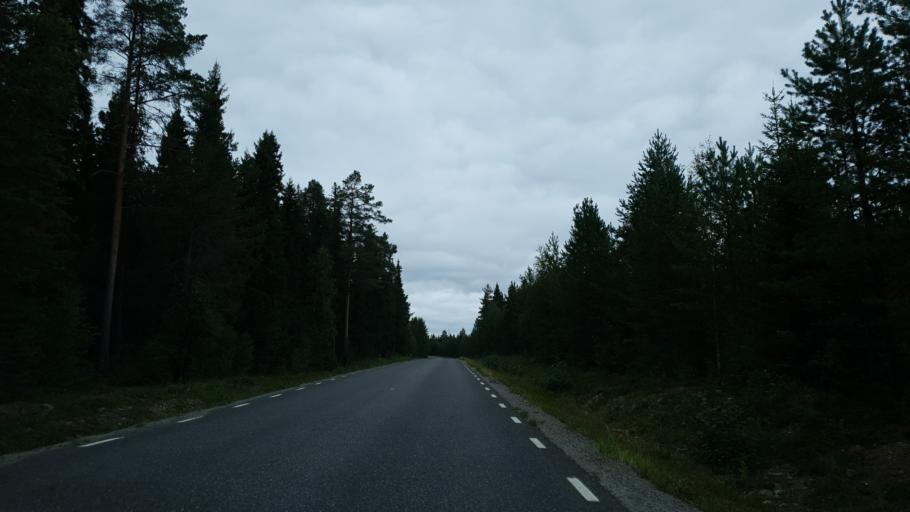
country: SE
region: Vaesterbotten
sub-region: Skelleftea Kommun
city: Viken
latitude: 64.8037
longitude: 20.7463
